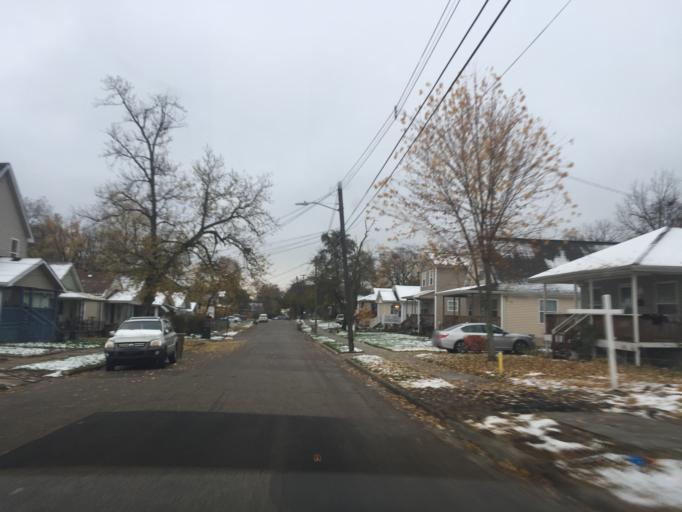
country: US
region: Michigan
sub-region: Oakland County
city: Pontiac
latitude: 42.6225
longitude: -83.2750
